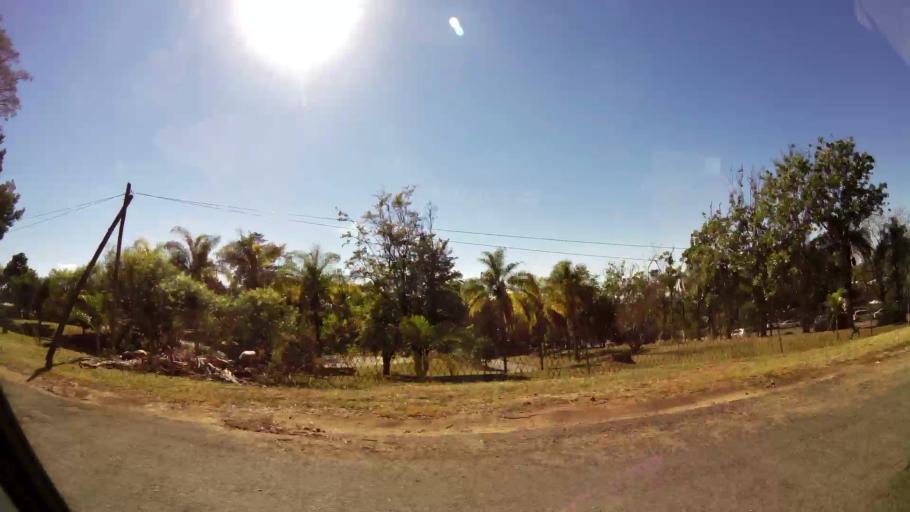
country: ZA
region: Limpopo
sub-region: Mopani District Municipality
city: Tzaneen
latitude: -23.8402
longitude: 30.1508
